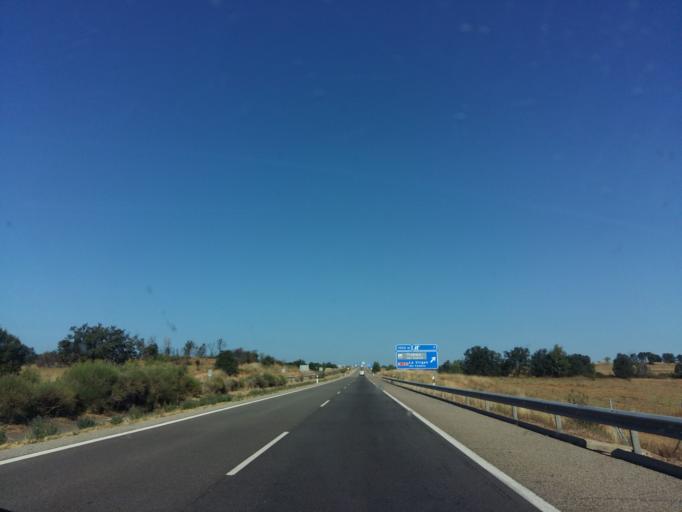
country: ES
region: Castille and Leon
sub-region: Provincia de Leon
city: San Andres del Rabanedo
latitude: 42.5702
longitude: -5.6039
